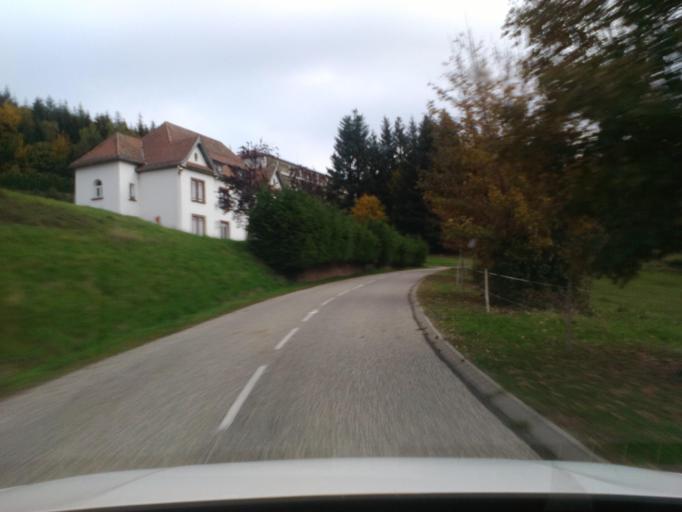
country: FR
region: Lorraine
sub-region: Departement des Vosges
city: Ban-de-Laveline
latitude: 48.3596
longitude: 7.1026
